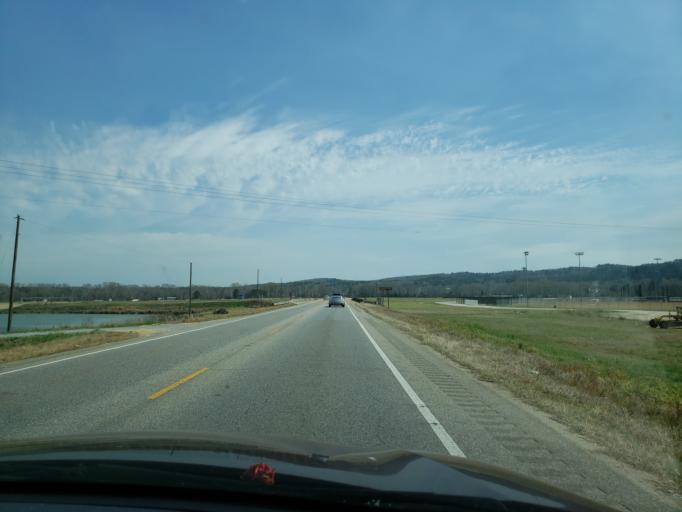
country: US
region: Alabama
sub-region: Elmore County
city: Wetumpka
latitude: 32.5534
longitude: -86.2073
